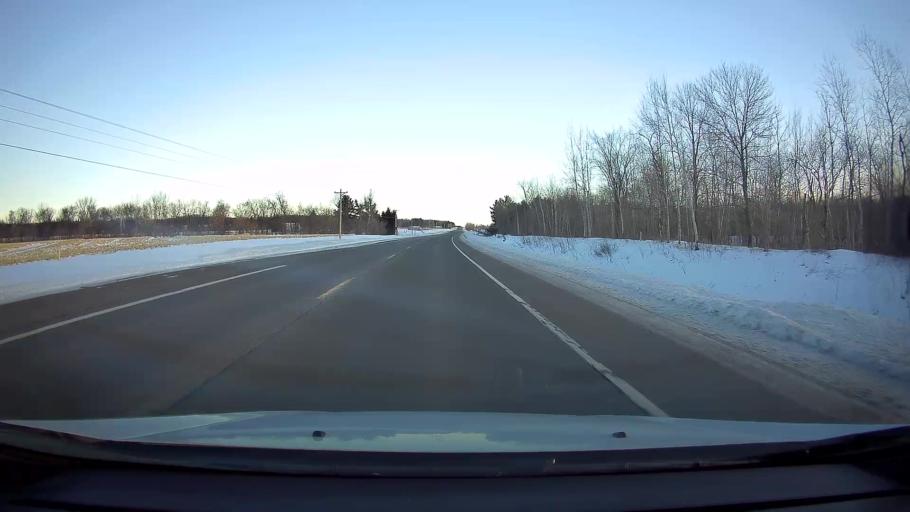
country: US
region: Wisconsin
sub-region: Barron County
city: Cumberland
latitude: 45.6112
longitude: -92.0098
